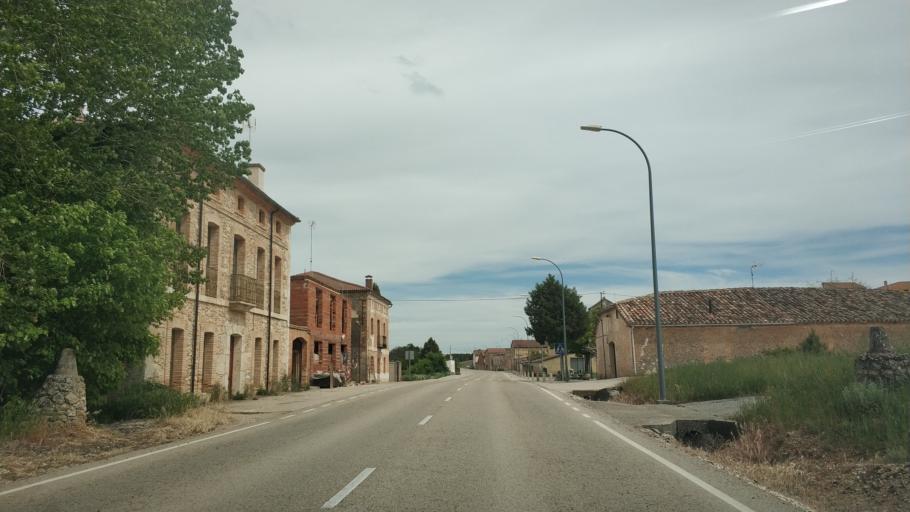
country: ES
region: Castille and Leon
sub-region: Provincia de Soria
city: Valdenebro
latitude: 41.5712
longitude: -3.0126
